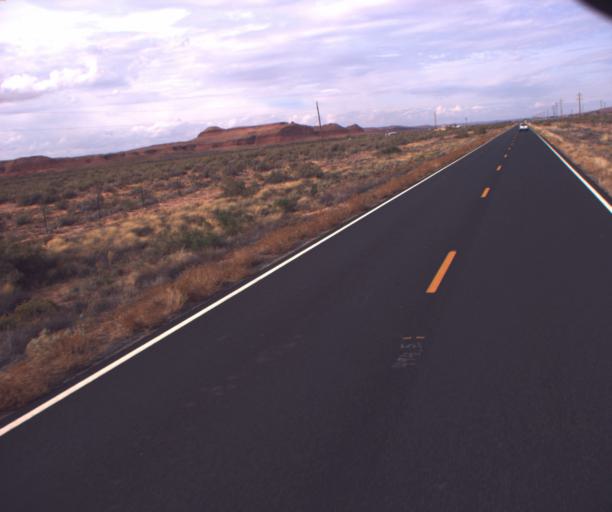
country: US
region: Arizona
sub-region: Apache County
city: Many Farms
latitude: 36.6967
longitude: -109.6138
